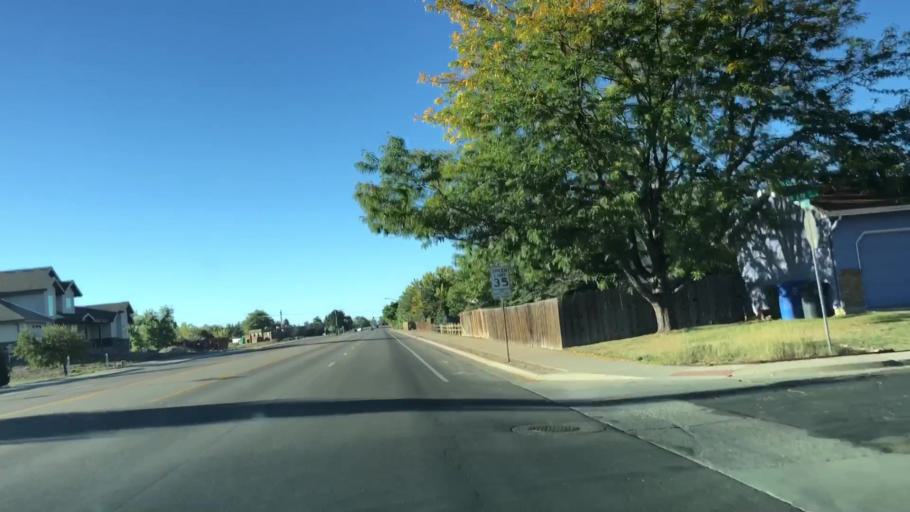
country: US
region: Colorado
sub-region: Larimer County
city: Loveland
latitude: 40.3865
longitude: -105.1160
